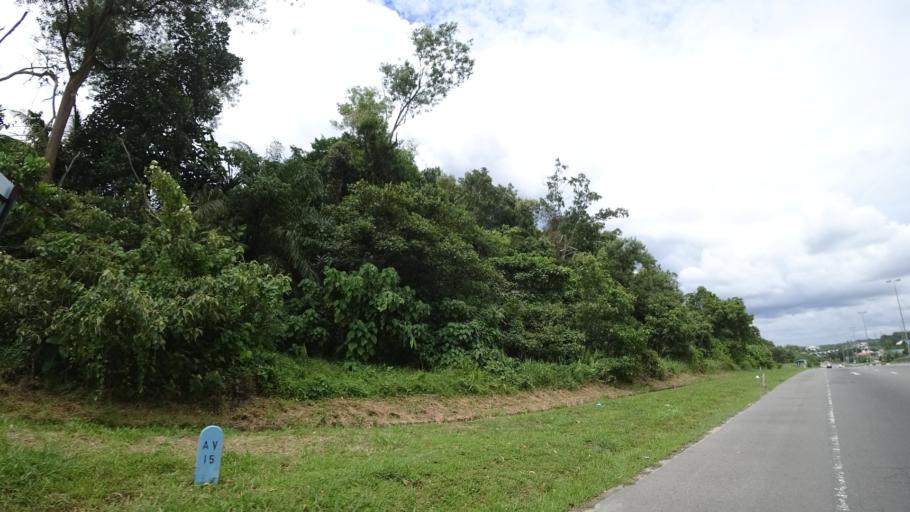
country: BN
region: Brunei and Muara
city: Bandar Seri Begawan
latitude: 4.8794
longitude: 114.8810
